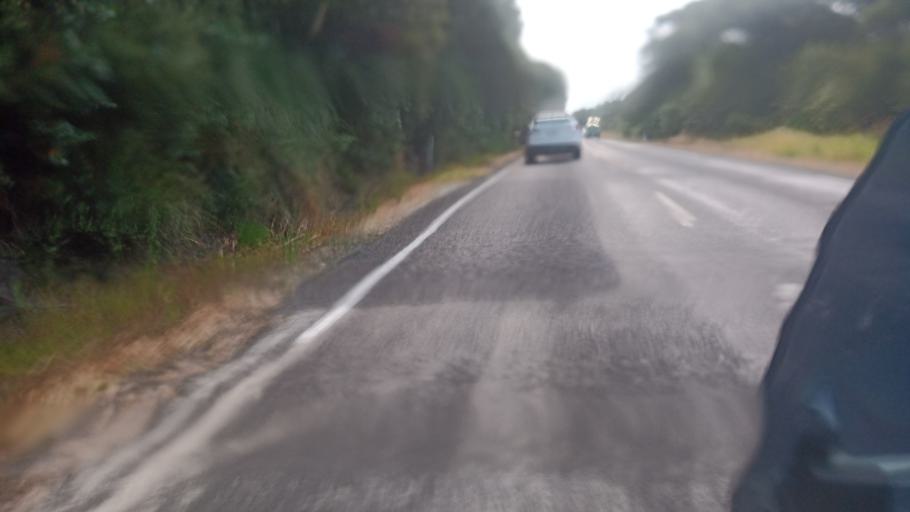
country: NZ
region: Bay of Plenty
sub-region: Opotiki District
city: Opotiki
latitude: -37.8019
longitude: 177.6637
